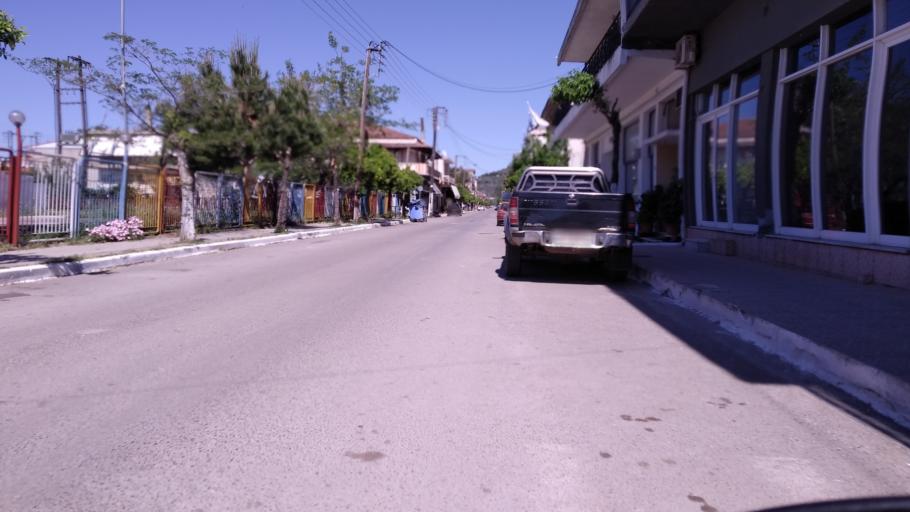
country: GR
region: Central Greece
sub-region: Nomos Fthiotidos
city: Malesina
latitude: 38.6233
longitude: 23.2334
